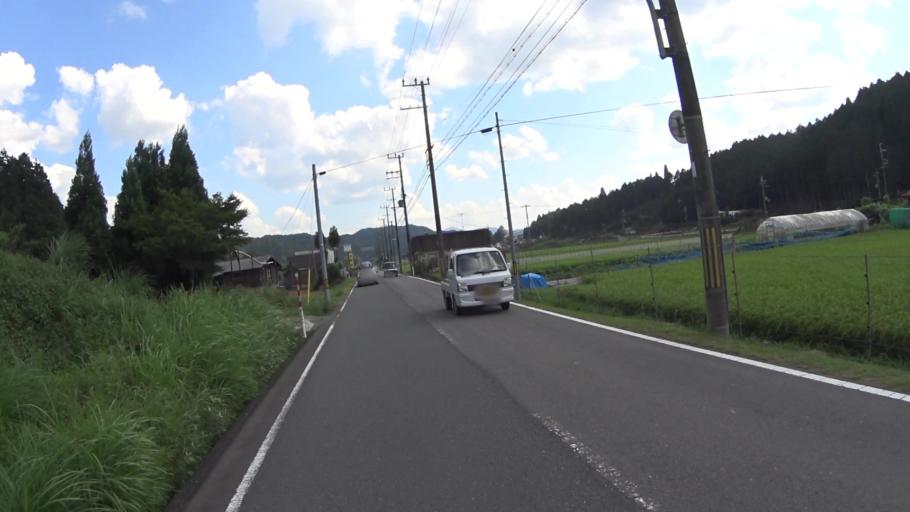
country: JP
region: Kyoto
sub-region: Kyoto-shi
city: Kamigyo-ku
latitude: 35.2099
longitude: 135.6414
